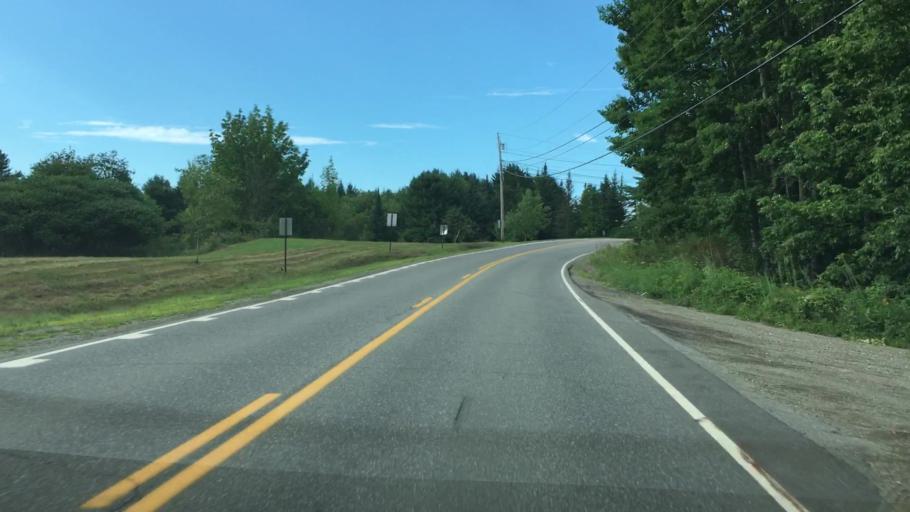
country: US
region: Maine
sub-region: Waldo County
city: Belfast
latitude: 44.4052
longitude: -69.0307
